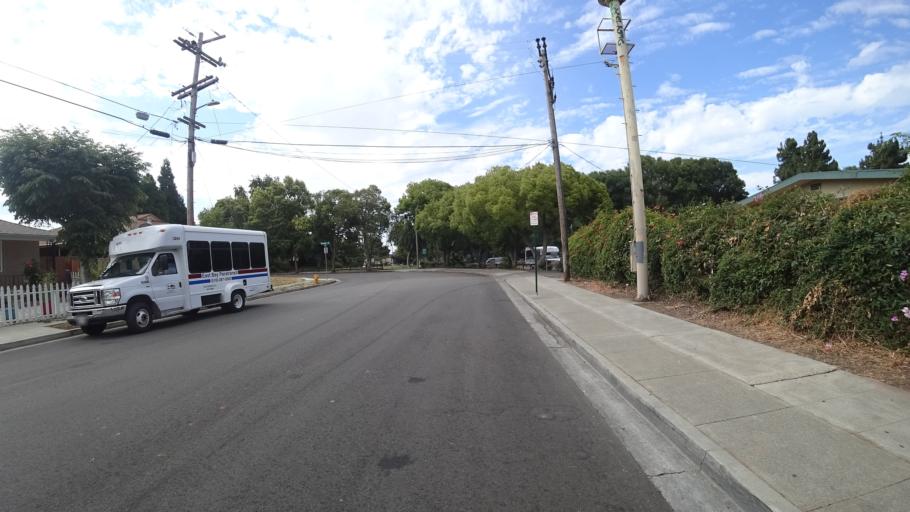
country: US
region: California
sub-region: Alameda County
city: Hayward
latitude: 37.6442
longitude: -122.0707
